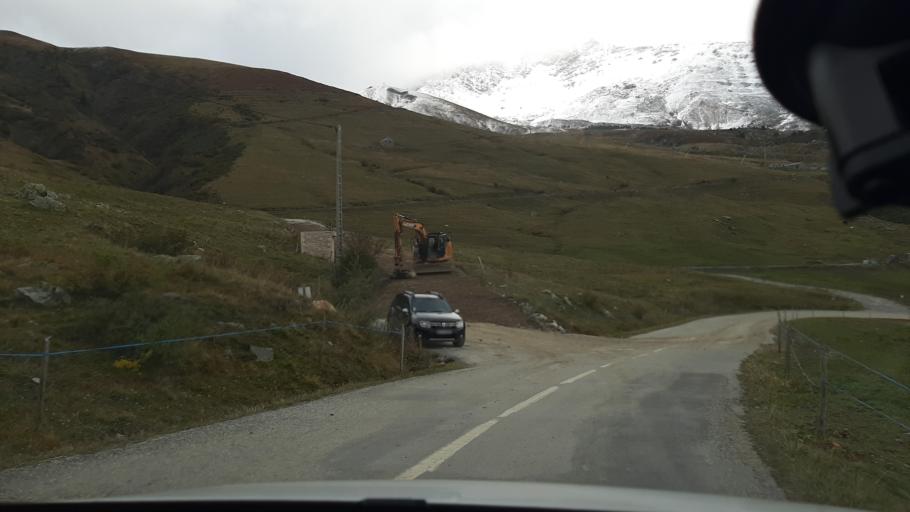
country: FR
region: Rhone-Alpes
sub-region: Departement de la Savoie
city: La Chambre
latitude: 45.4263
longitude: 6.3730
